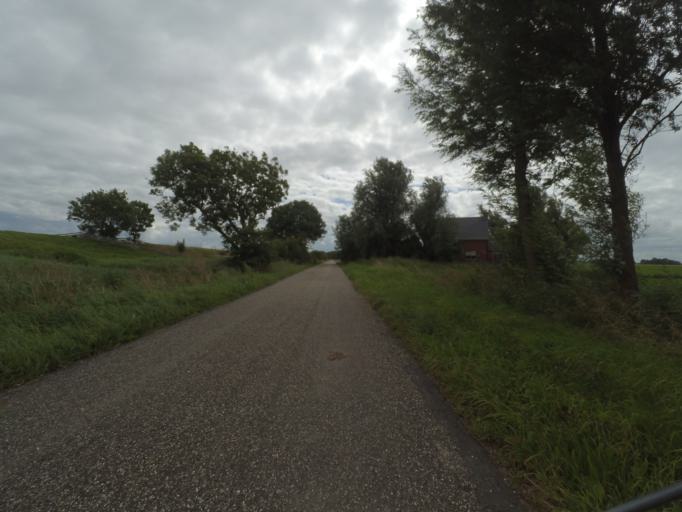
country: NL
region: Friesland
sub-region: Gemeente Dongeradeel
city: Anjum
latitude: 53.3352
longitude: 6.1536
